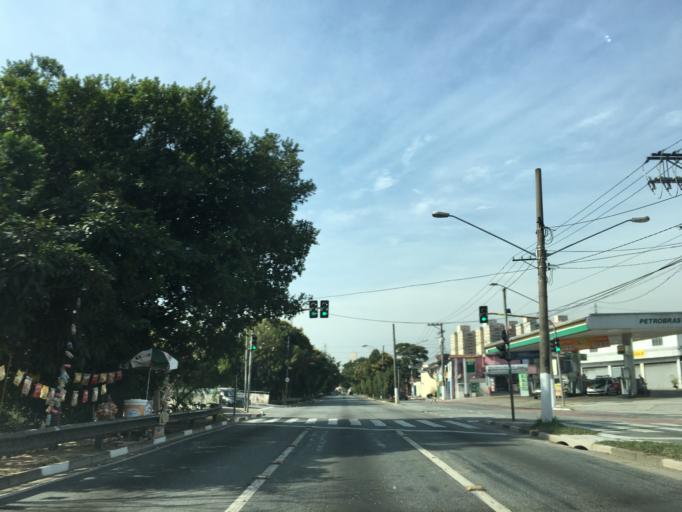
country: BR
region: Sao Paulo
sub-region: Osasco
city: Osasco
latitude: -23.5703
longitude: -46.7620
